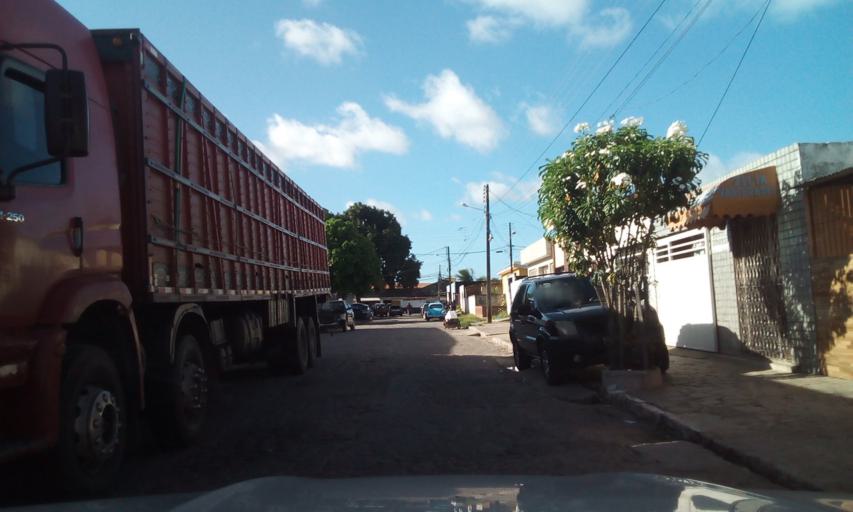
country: BR
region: Paraiba
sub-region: Bayeux
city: Bayeux
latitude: -7.1516
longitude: -34.8935
